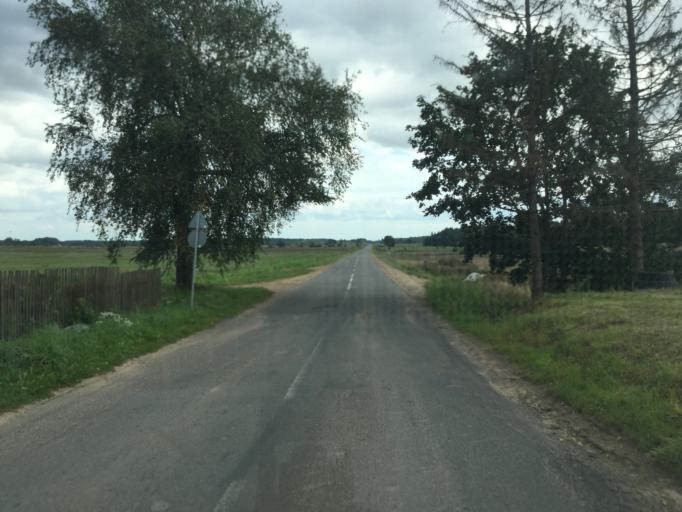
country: BY
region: Vitebsk
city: Vitebsk
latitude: 55.1431
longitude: 30.2872
